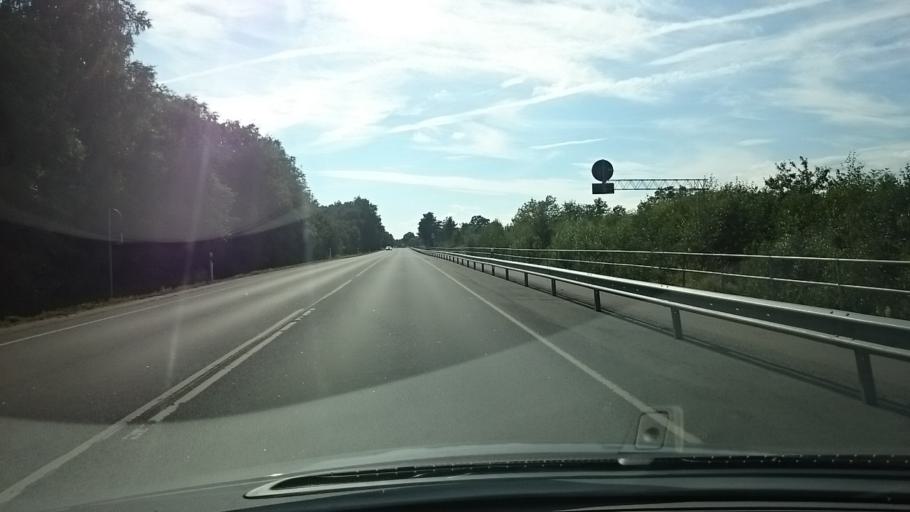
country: EE
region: Laeaene
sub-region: Ridala Parish
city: Uuemoisa
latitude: 58.9489
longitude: 23.6350
